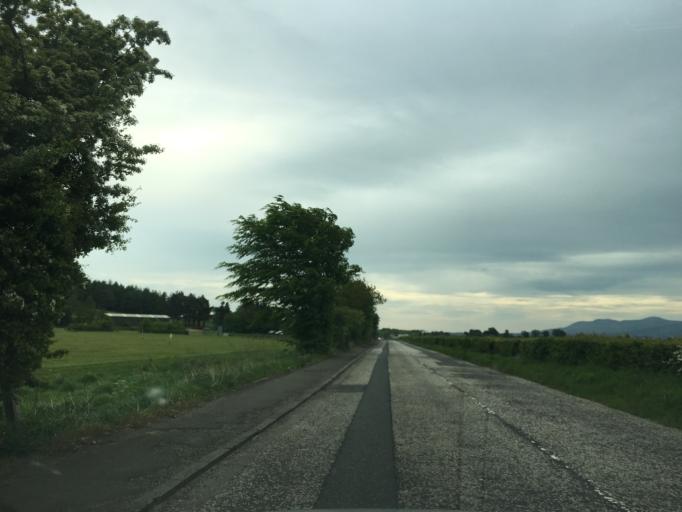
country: GB
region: Scotland
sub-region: Edinburgh
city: Ratho
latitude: 55.9512
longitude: -3.3400
